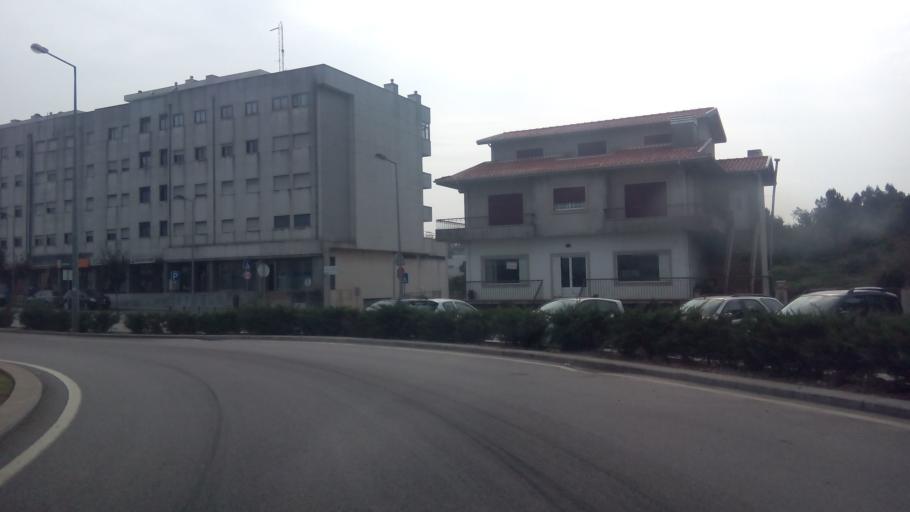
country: PT
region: Porto
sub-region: Paredes
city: Gandra
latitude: 41.1822
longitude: -8.4437
